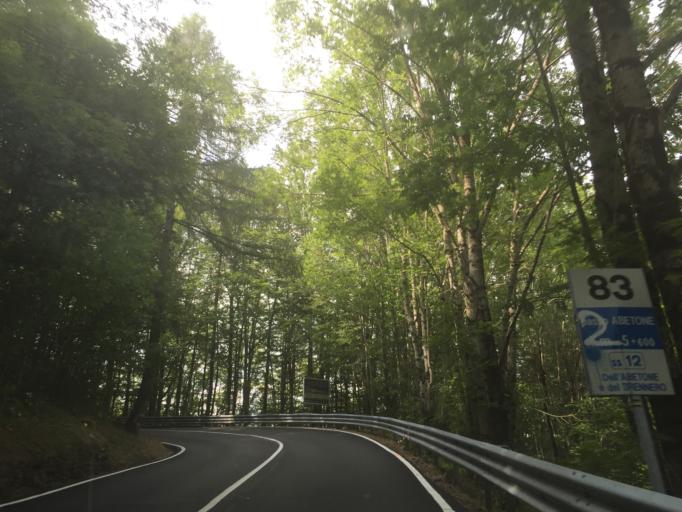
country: IT
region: Tuscany
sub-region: Provincia di Pistoia
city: Cutigliano
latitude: 44.1235
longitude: 10.7147
